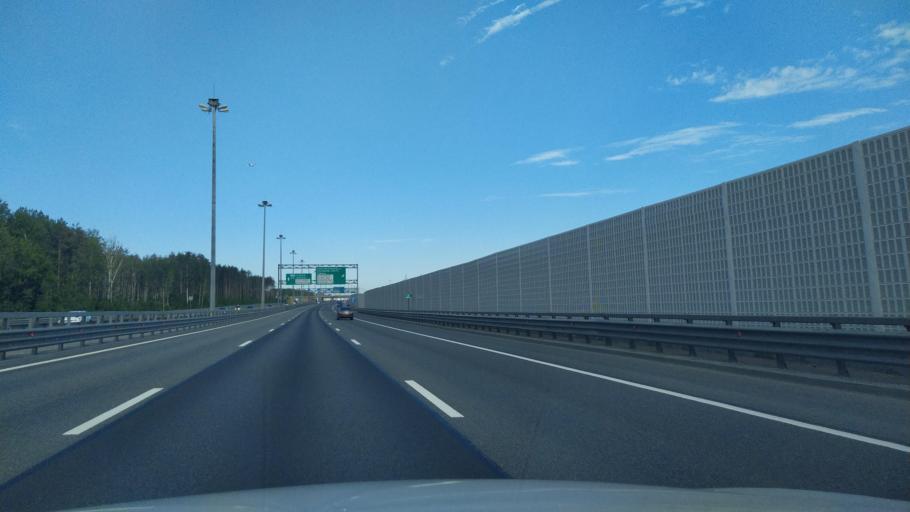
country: RU
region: St.-Petersburg
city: Strel'na
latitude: 59.8157
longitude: 30.0590
